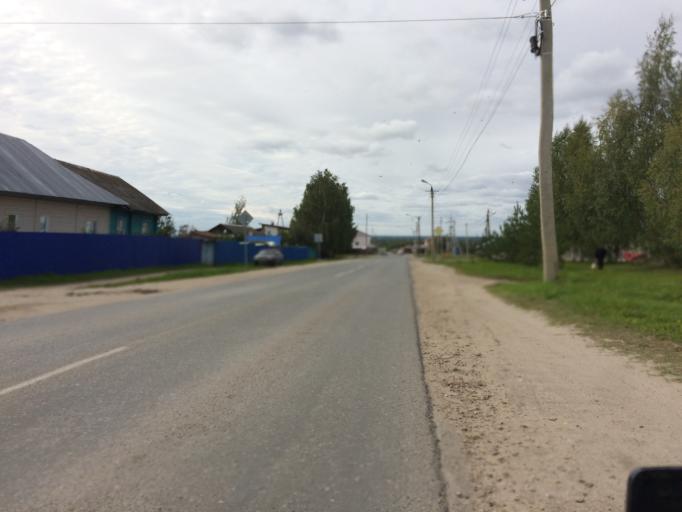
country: RU
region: Mariy-El
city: Yoshkar-Ola
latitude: 56.6565
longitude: 47.9747
